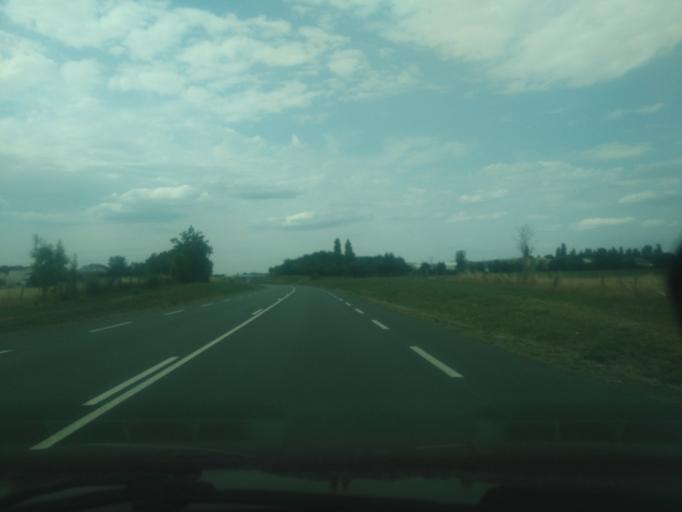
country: FR
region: Pays de la Loire
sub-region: Departement de la Vendee
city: Chantonnay
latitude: 46.6931
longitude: -1.0387
